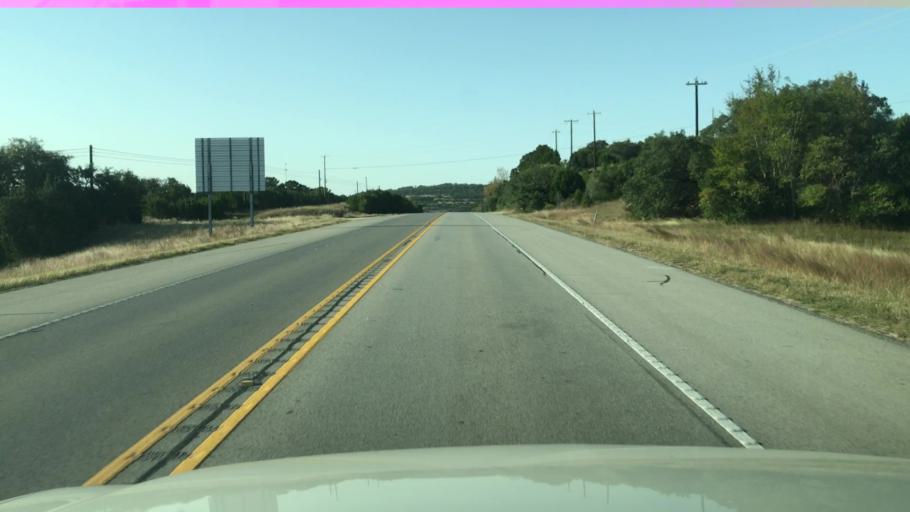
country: US
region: Texas
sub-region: Blanco County
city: Johnson City
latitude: 30.1919
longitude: -98.3770
